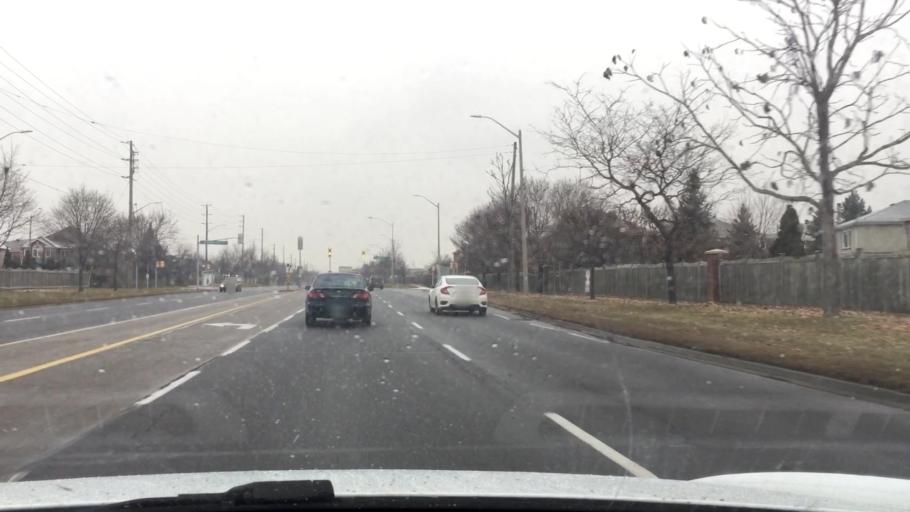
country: CA
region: Ontario
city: Markham
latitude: 43.8373
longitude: -79.2768
